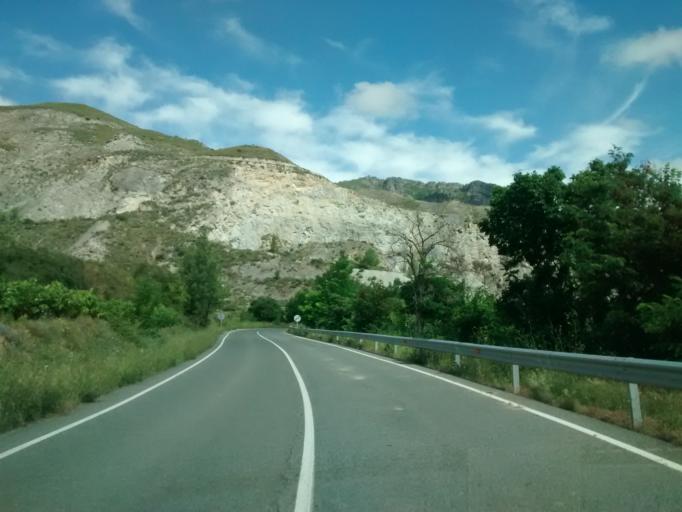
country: ES
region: La Rioja
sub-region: Provincia de La Rioja
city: Leza de Rio Leza
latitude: 42.3355
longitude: -2.4083
